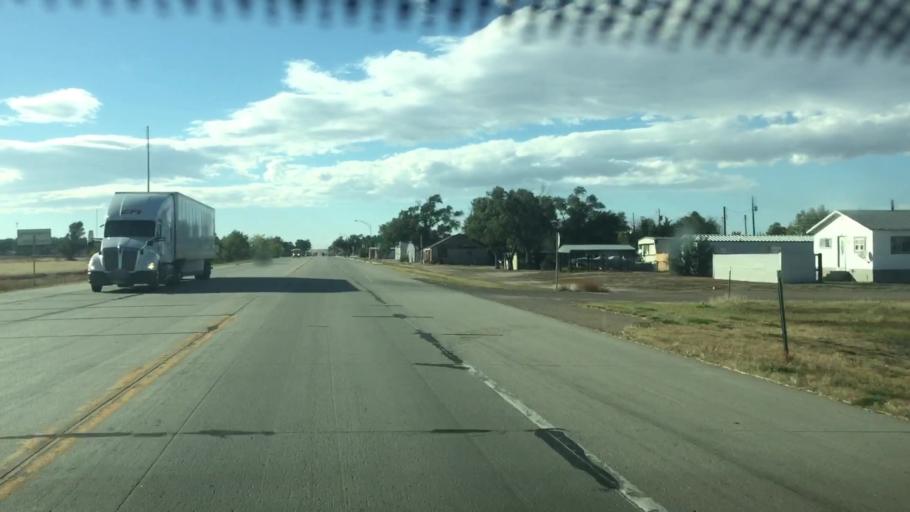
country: US
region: Colorado
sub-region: Lincoln County
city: Hugo
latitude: 39.1311
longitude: -103.4600
